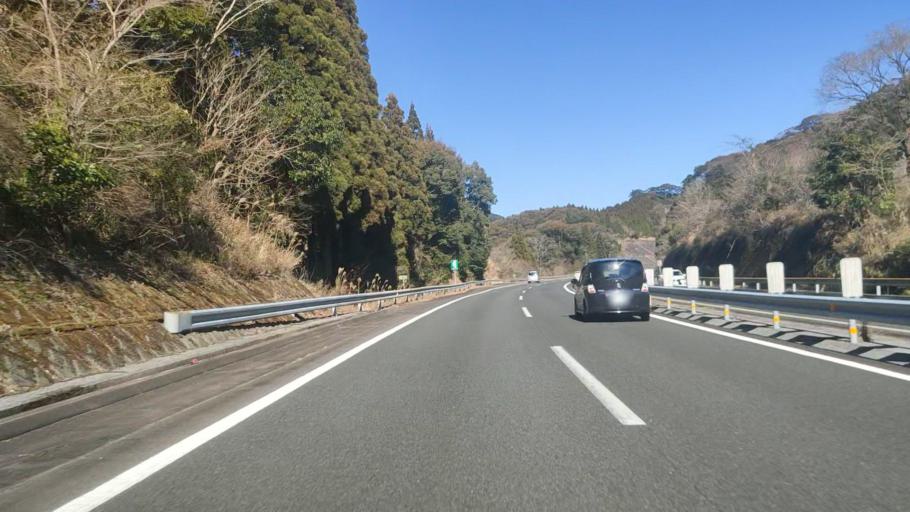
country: JP
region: Miyazaki
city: Miyakonojo
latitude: 31.8178
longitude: 131.2164
